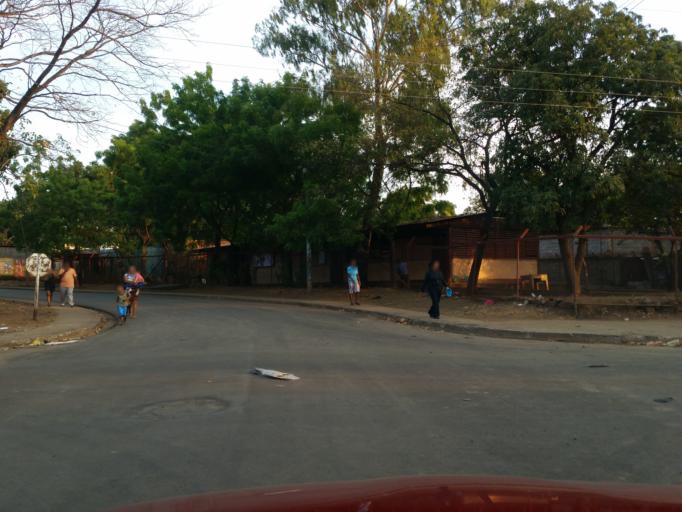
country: NI
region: Managua
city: Managua
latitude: 12.1354
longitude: -86.2634
